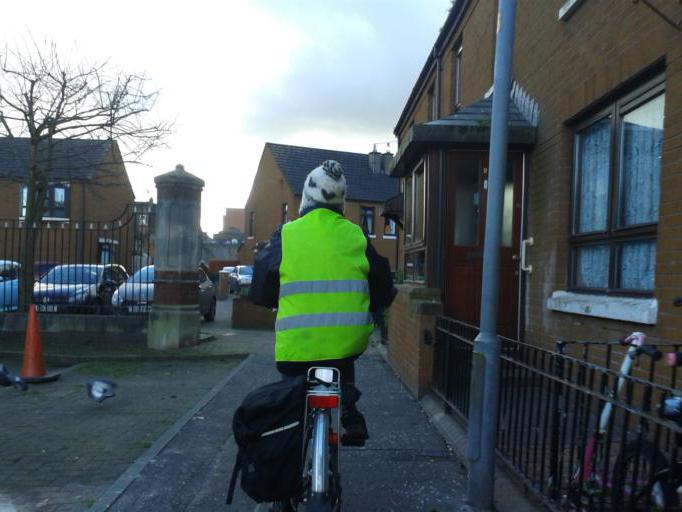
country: GB
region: Northern Ireland
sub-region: City of Belfast
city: Belfast
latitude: 54.5945
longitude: -5.9251
